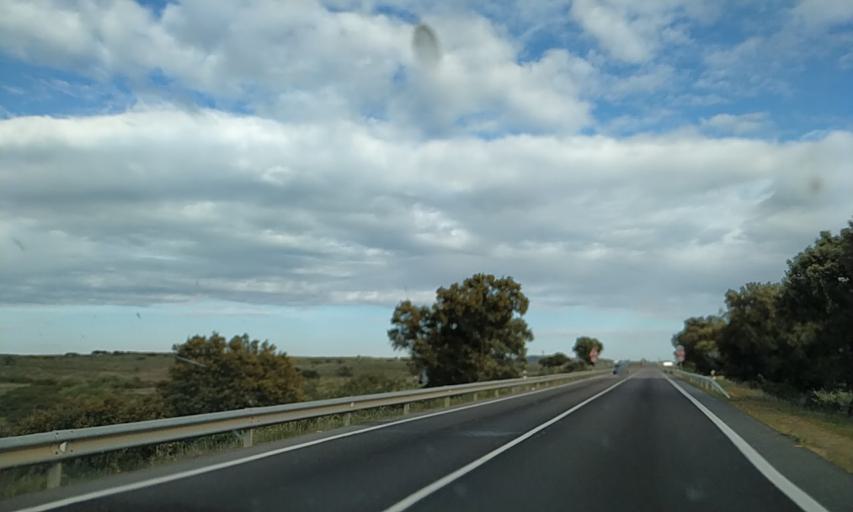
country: ES
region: Extremadura
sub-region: Provincia de Caceres
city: Huelaga
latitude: 40.0322
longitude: -6.6159
